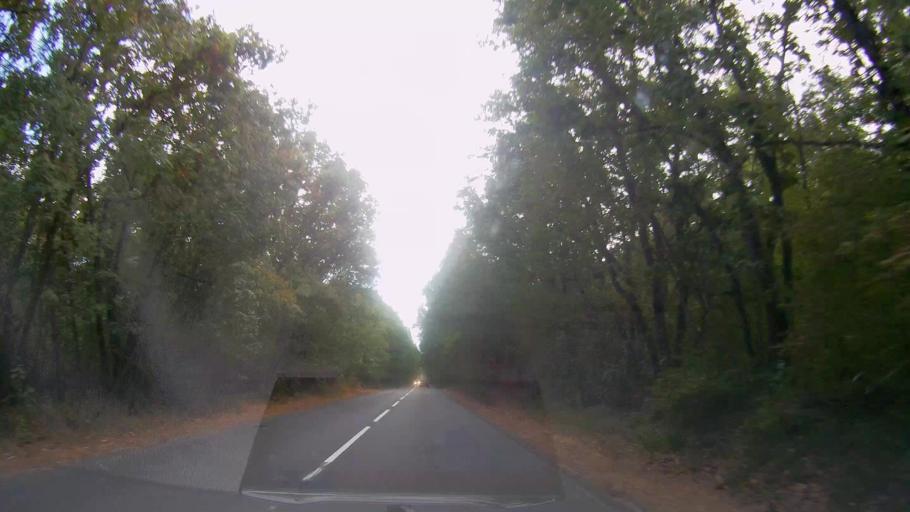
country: BG
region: Burgas
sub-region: Obshtina Primorsko
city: Primorsko
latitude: 42.2891
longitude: 27.7351
